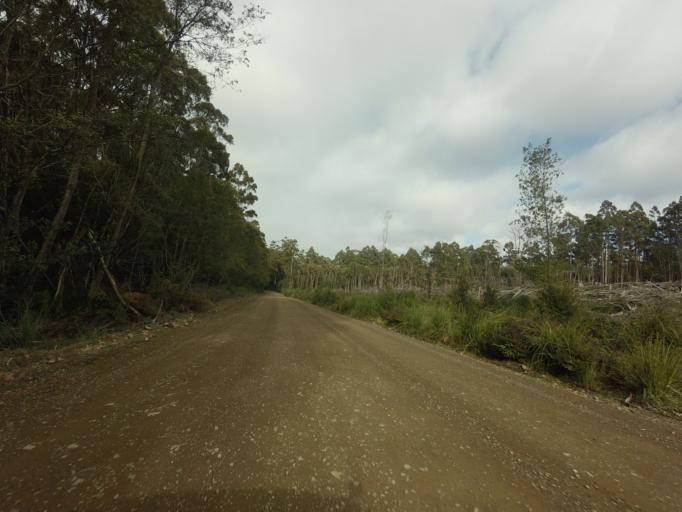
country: AU
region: Tasmania
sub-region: Huon Valley
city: Geeveston
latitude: -43.4892
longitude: 146.8885
